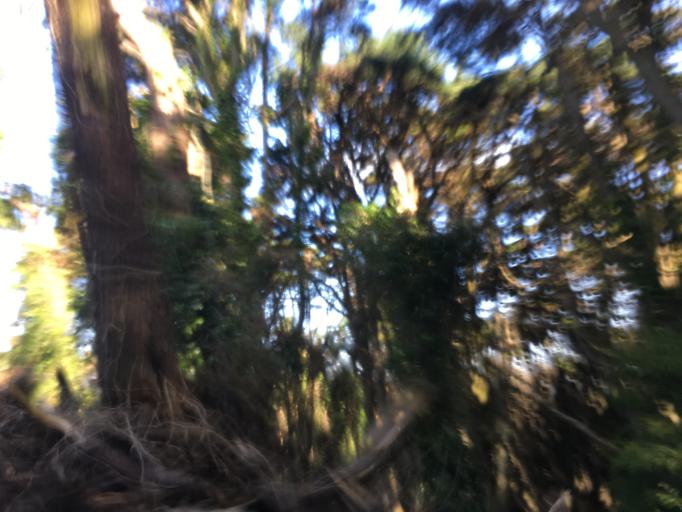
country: PT
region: Lisbon
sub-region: Sintra
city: Colares
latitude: 38.7723
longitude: -9.4579
